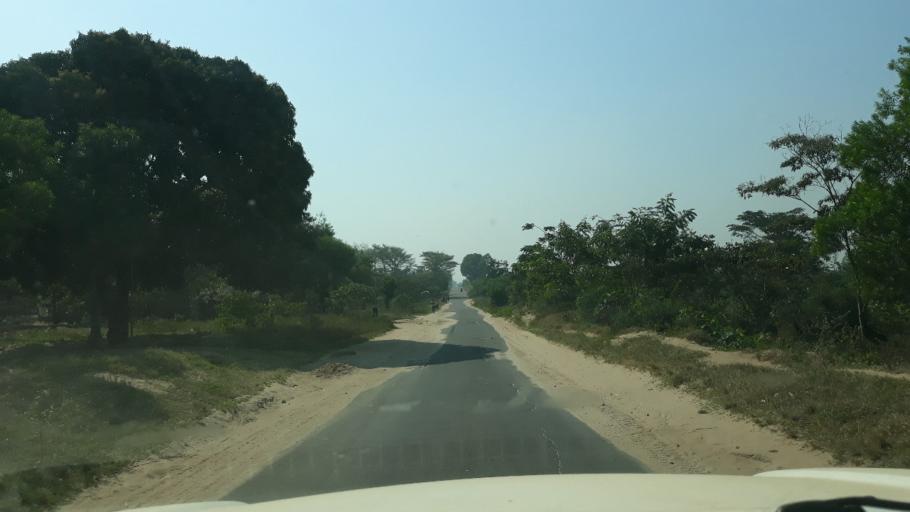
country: CD
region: South Kivu
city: Uvira
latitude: -3.2260
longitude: 29.1657
